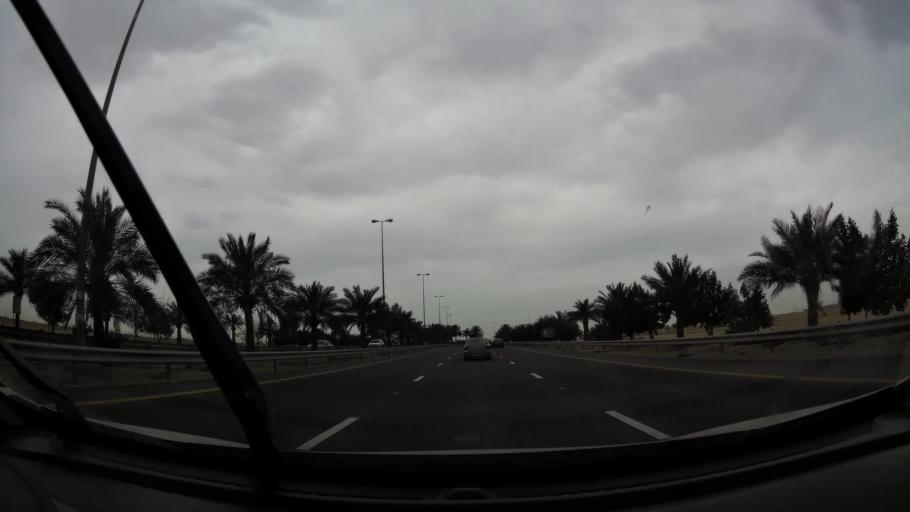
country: BH
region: Central Governorate
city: Dar Kulayb
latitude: 26.0812
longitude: 50.5397
